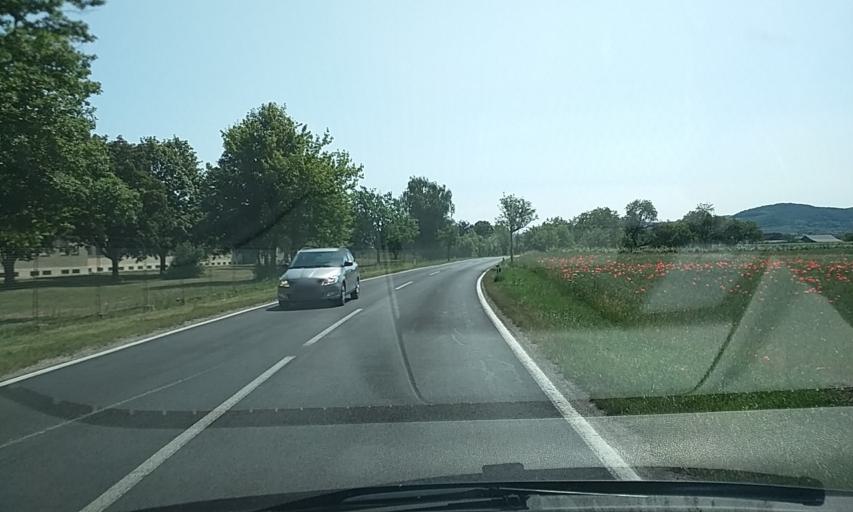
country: AT
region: Lower Austria
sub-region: Politischer Bezirk Krems
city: Weinzierl bei Krems
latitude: 48.3914
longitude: 15.5866
